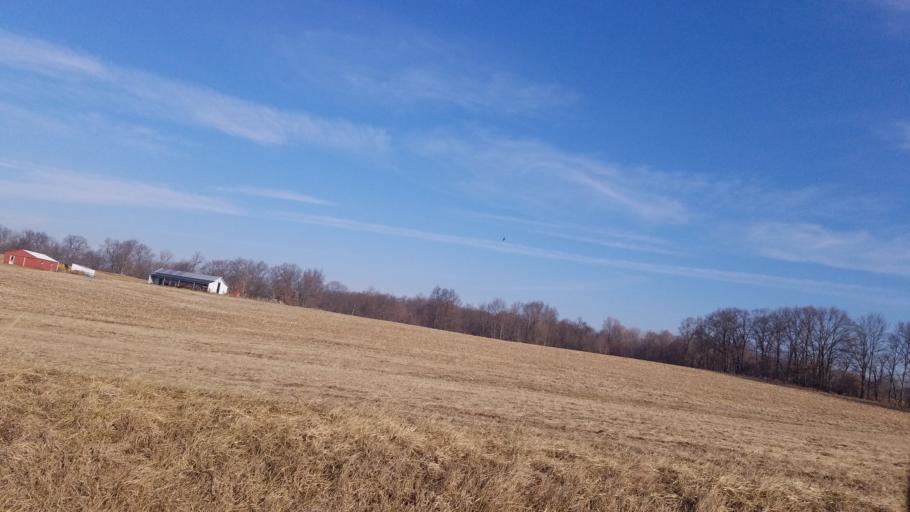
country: US
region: Ohio
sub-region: Knox County
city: Gambier
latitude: 40.4919
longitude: -82.3744
